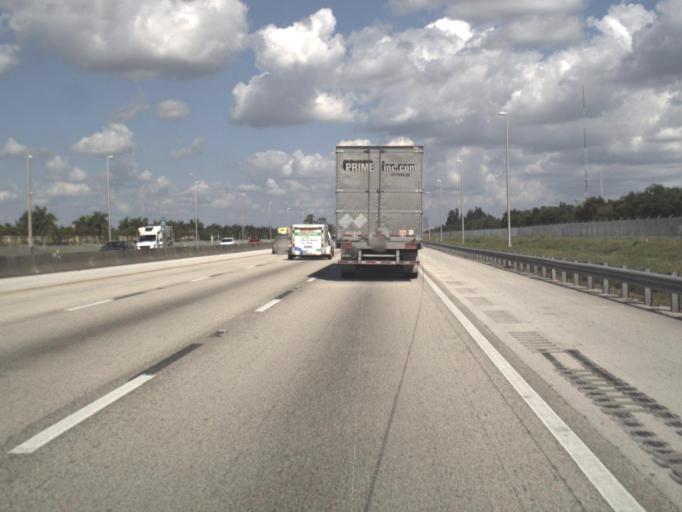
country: US
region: Florida
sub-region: Palm Beach County
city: Villages of Oriole
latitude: 26.5086
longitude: -80.1724
